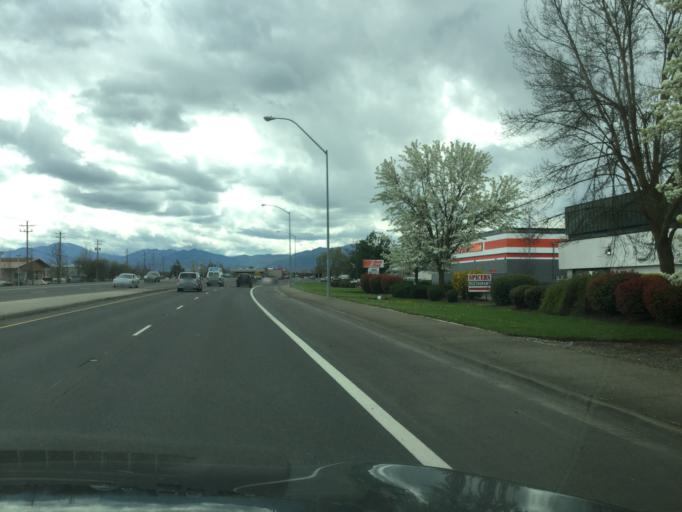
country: US
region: Oregon
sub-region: Jackson County
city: Medford
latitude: 42.3655
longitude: -122.8561
